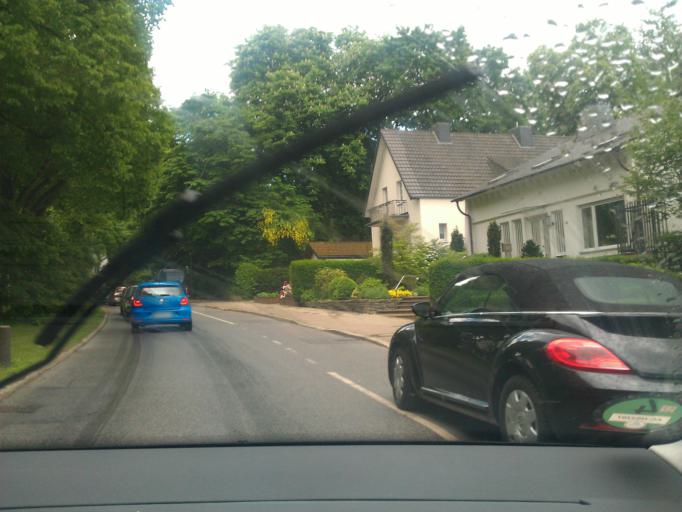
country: DE
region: North Rhine-Westphalia
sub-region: Regierungsbezirk Koln
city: Aachen
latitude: 50.7537
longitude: 6.0887
